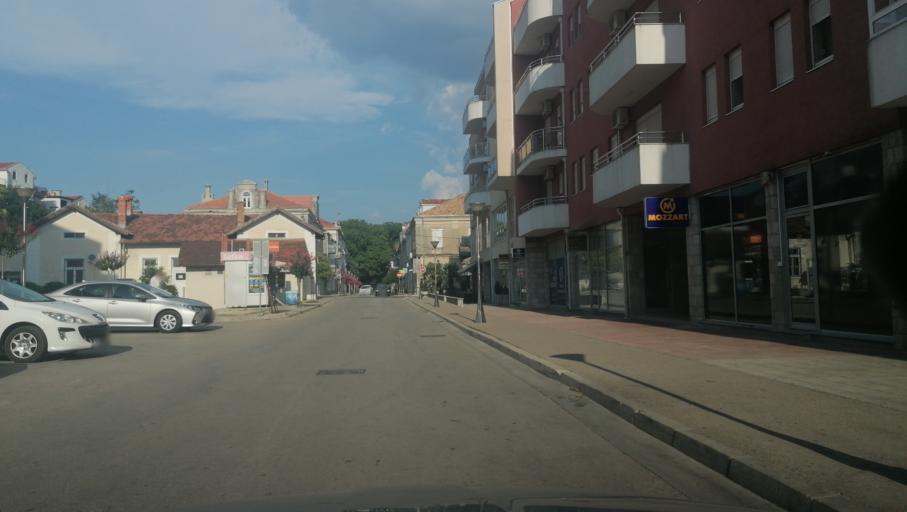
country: BA
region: Republika Srpska
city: Trebinje
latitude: 42.7111
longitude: 18.3416
